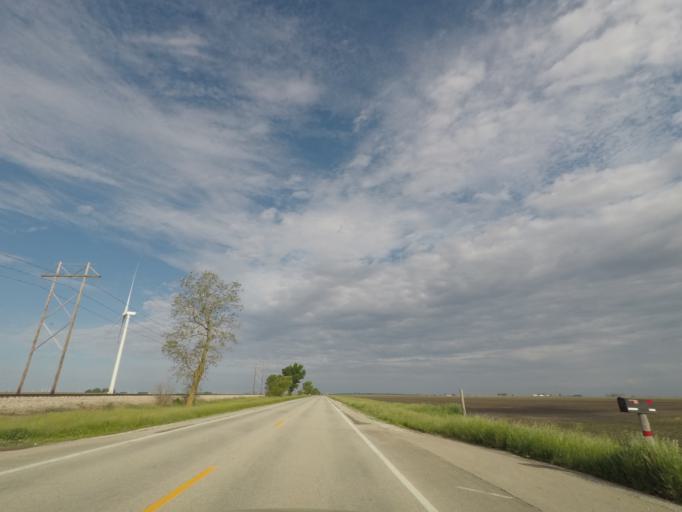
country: US
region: Illinois
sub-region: Logan County
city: Mount Pulaski
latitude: 39.9868
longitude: -89.2280
